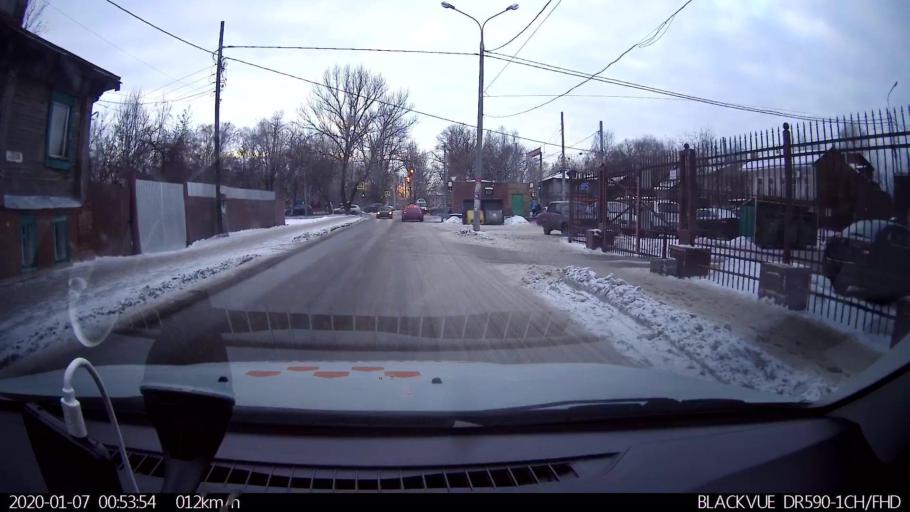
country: RU
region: Nizjnij Novgorod
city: Nizhniy Novgorod
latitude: 56.3229
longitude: 44.0393
